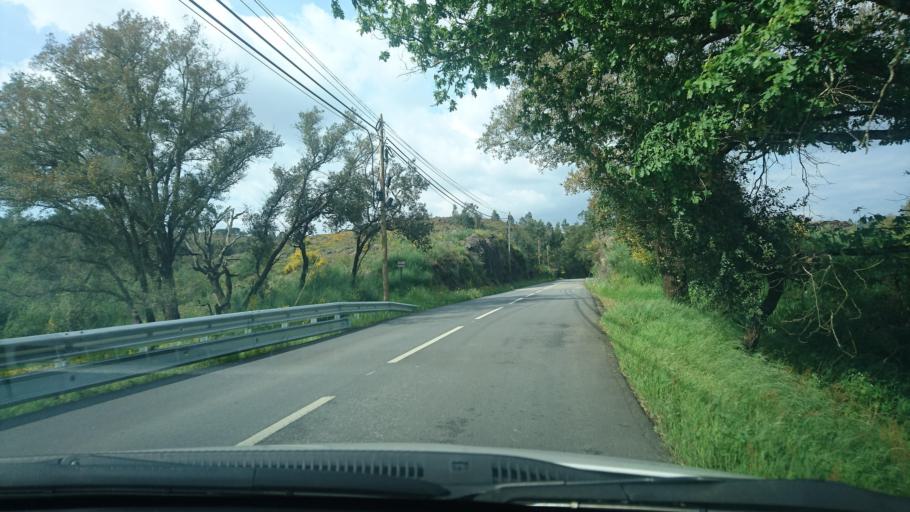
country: PT
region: Porto
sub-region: Paredes
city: Recarei
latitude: 41.1417
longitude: -8.4178
